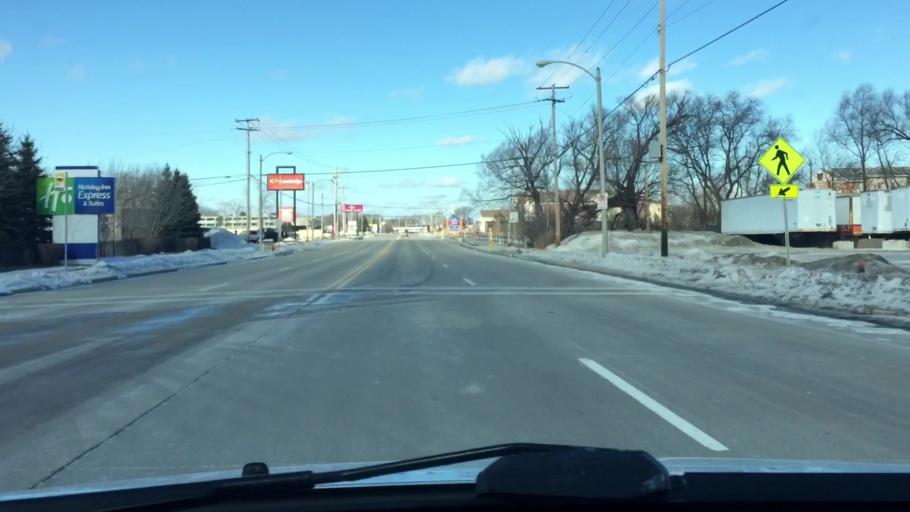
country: US
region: Wisconsin
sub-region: Milwaukee County
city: Greendale
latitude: 42.9252
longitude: -87.9304
